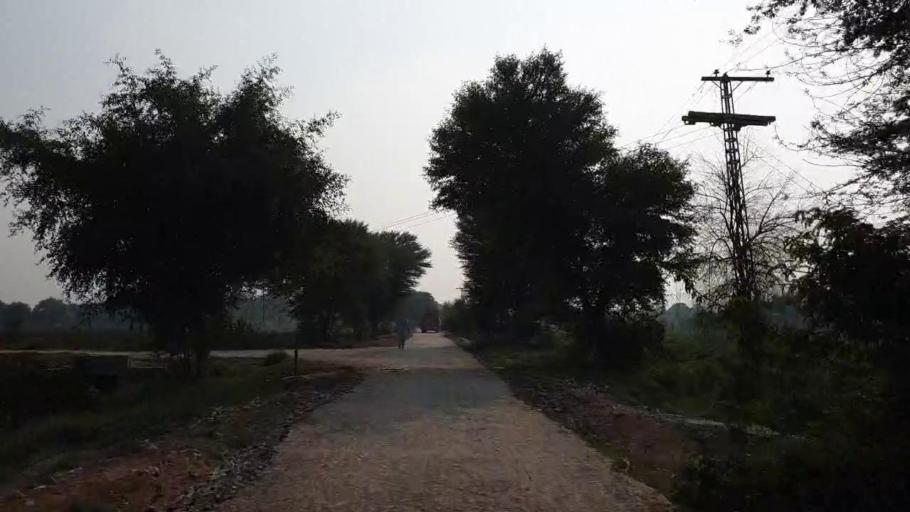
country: PK
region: Sindh
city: Bhan
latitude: 26.5834
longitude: 67.7305
